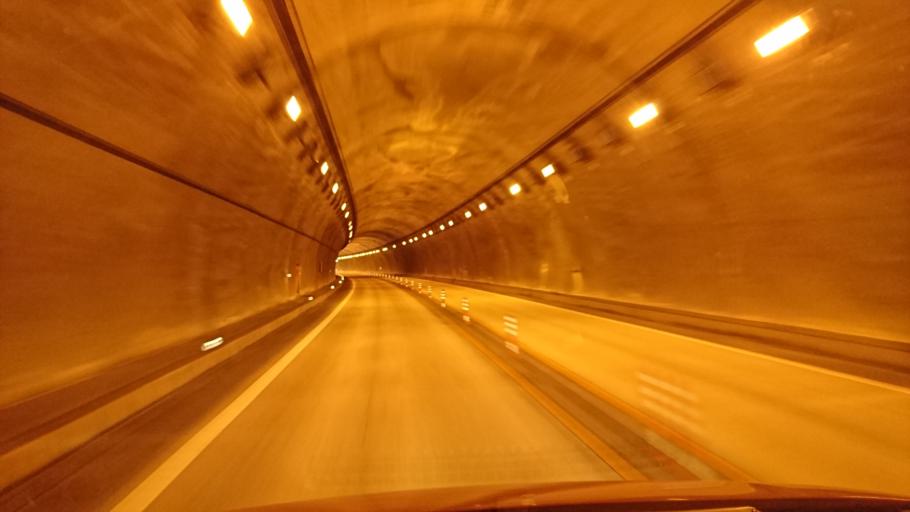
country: JP
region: Hiroshima
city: Innoshima
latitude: 34.1312
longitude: 133.0257
